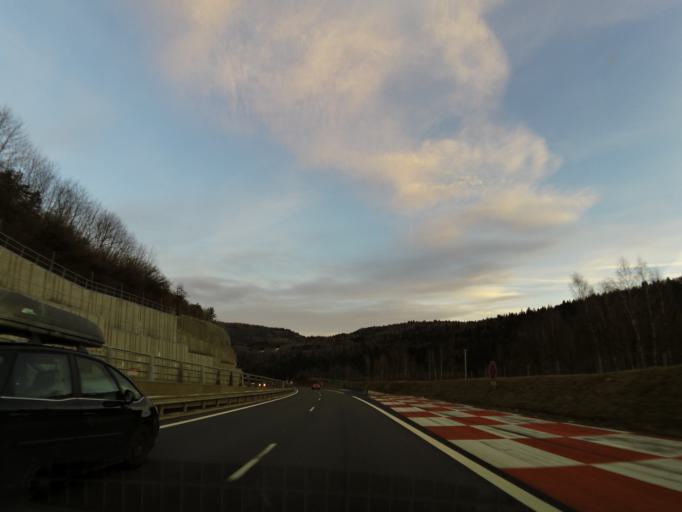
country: FR
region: Rhone-Alpes
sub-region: Departement de l'Ain
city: Nantua
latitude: 46.1655
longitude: 5.6963
